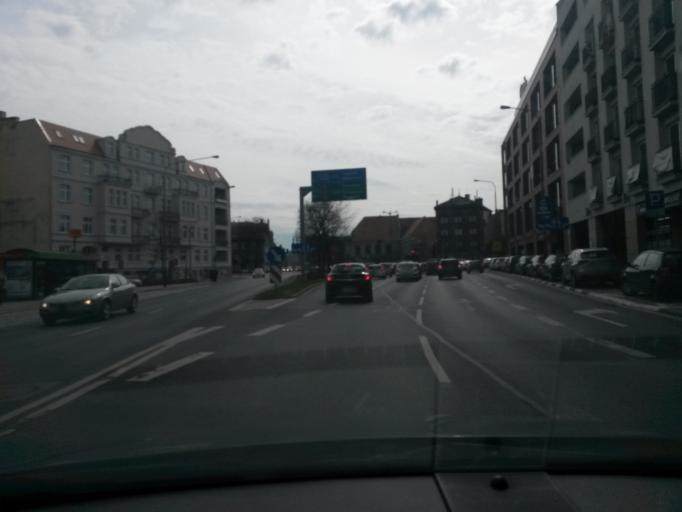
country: PL
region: Greater Poland Voivodeship
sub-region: Poznan
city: Poznan
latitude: 52.4121
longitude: 16.9387
